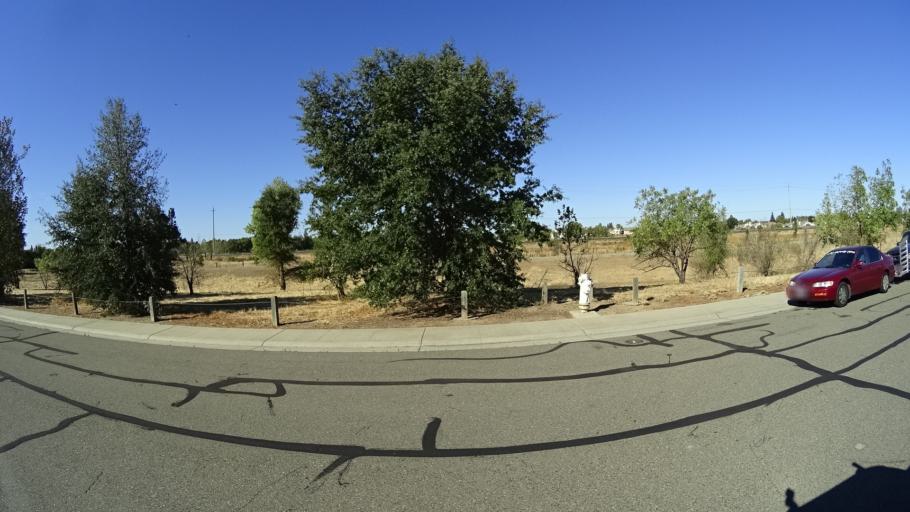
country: US
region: California
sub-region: Sacramento County
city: Vineyard
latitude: 38.4478
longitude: -121.3777
